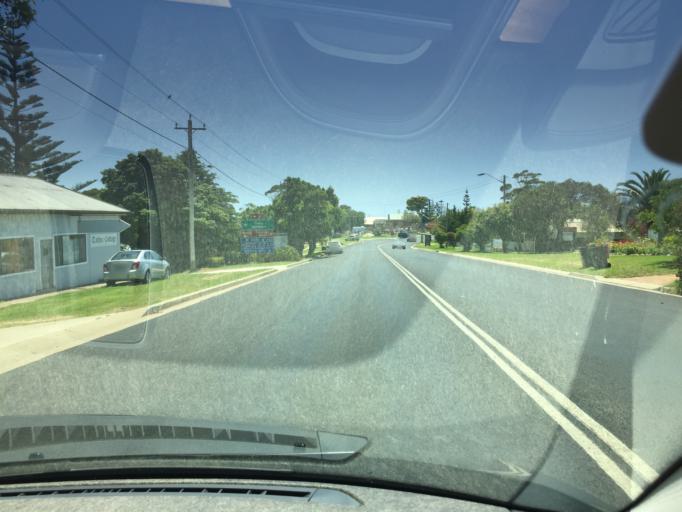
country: AU
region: New South Wales
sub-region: Bega Valley
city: Bega
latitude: -36.7309
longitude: 149.9844
